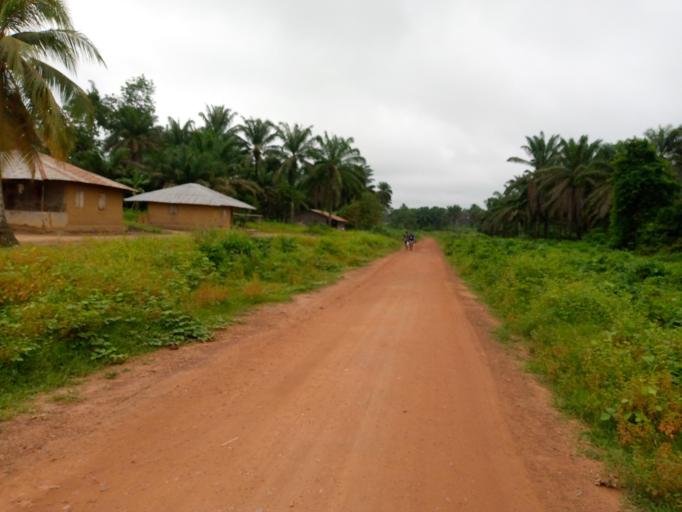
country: SL
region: Southern Province
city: Sumbuya
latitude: 7.5941
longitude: -12.0846
